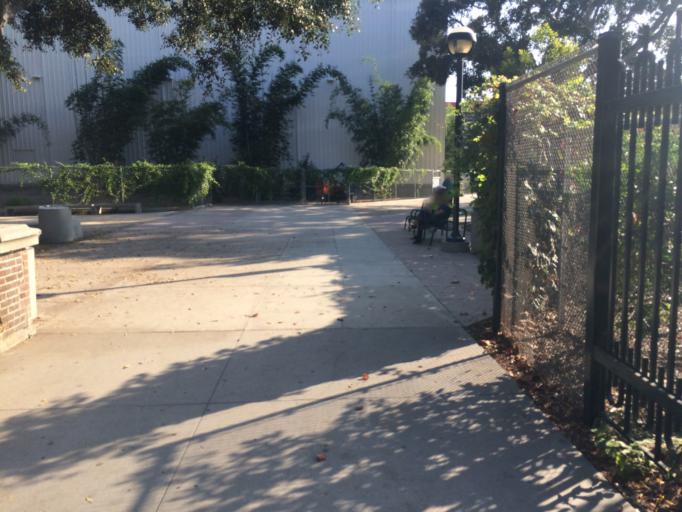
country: US
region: California
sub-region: Los Angeles County
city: Los Angeles
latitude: 34.0167
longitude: -118.2876
